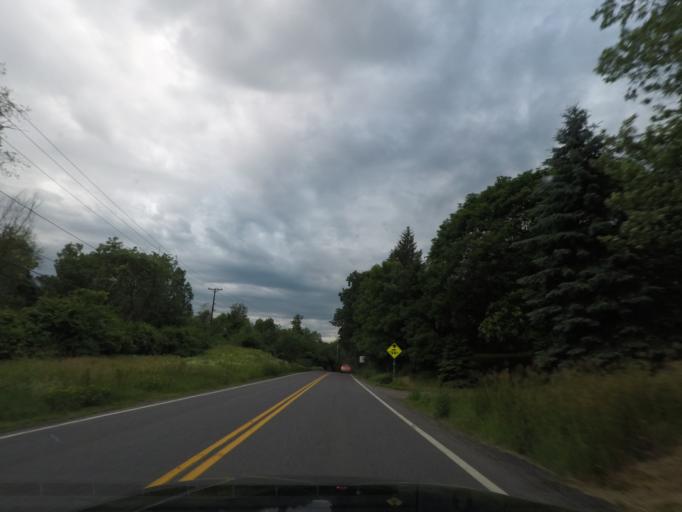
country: US
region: New York
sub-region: Dutchess County
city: Pine Plains
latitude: 41.9557
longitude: -73.7507
